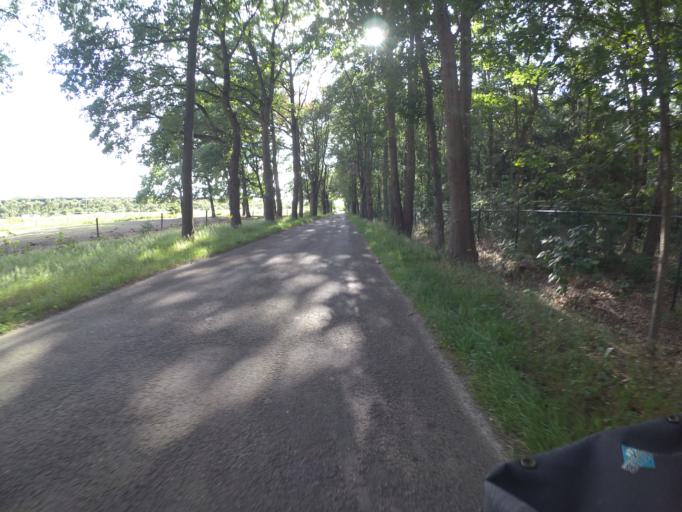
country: NL
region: North Brabant
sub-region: Gemeente Eindhoven
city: Lakerlopen
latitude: 51.4062
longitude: 5.4872
